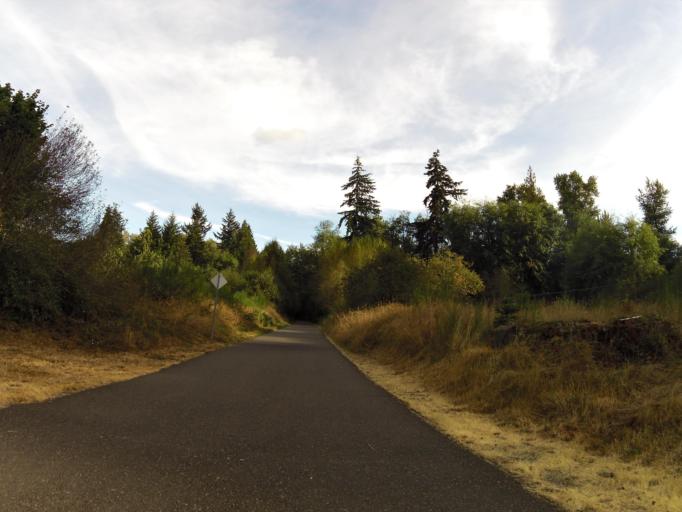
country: US
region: Washington
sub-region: Thurston County
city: Lacey
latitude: 46.9820
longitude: -122.8243
